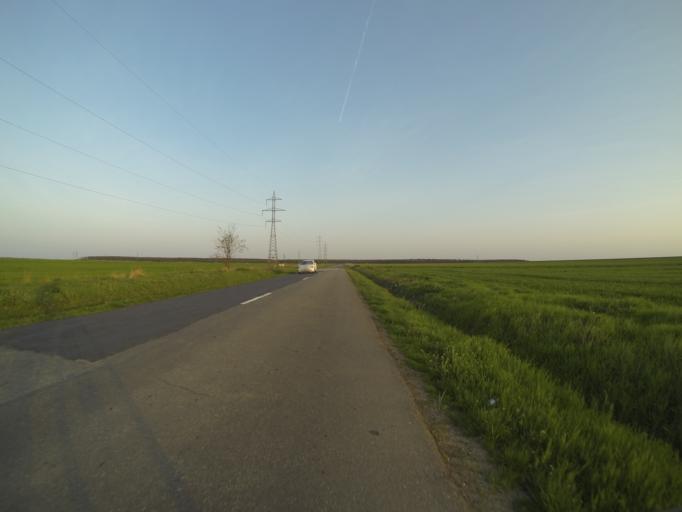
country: RO
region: Dolj
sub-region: Comuna Segarcea
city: Segarcea
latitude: 44.0736
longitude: 23.7943
